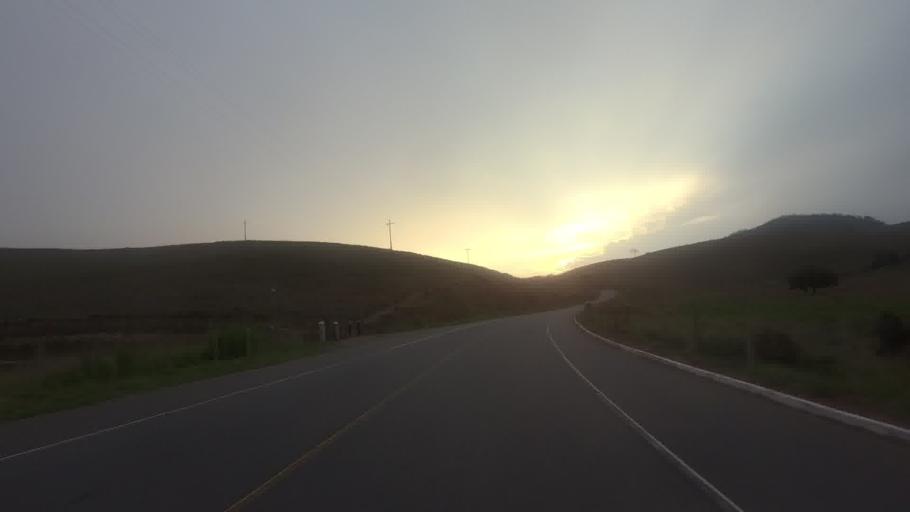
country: BR
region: Rio de Janeiro
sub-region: Carmo
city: Carmo
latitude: -21.7595
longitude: -42.4902
